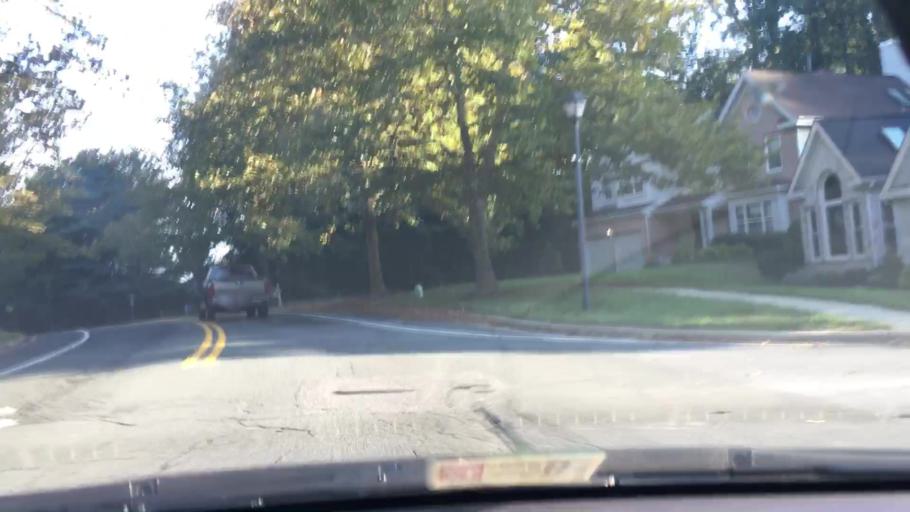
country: US
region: Maryland
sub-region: Montgomery County
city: Olney
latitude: 39.1508
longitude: -77.0500
